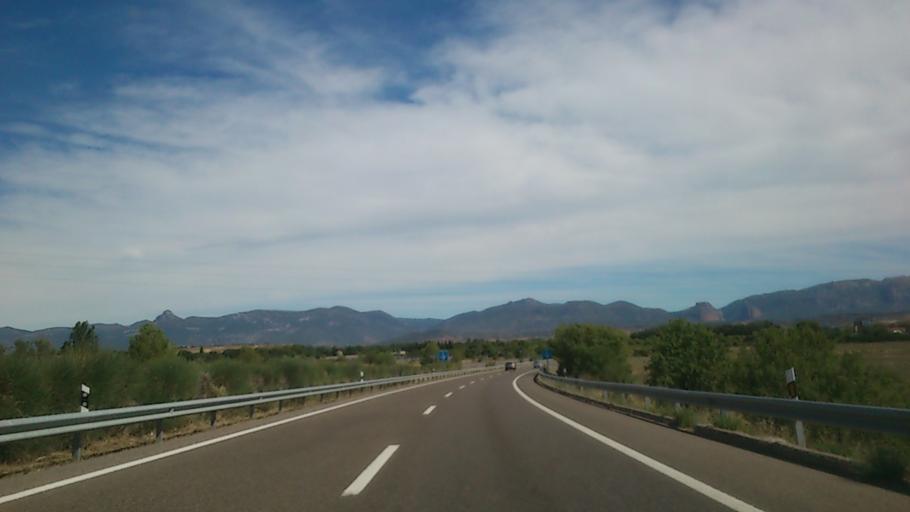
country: ES
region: Aragon
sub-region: Provincia de Huesca
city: Huesca
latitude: 42.1409
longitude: -0.4312
